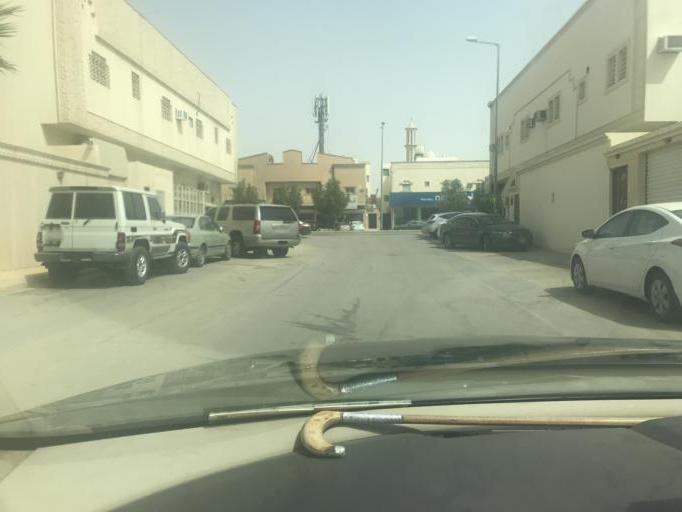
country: SA
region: Ar Riyad
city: Riyadh
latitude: 24.7424
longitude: 46.7875
